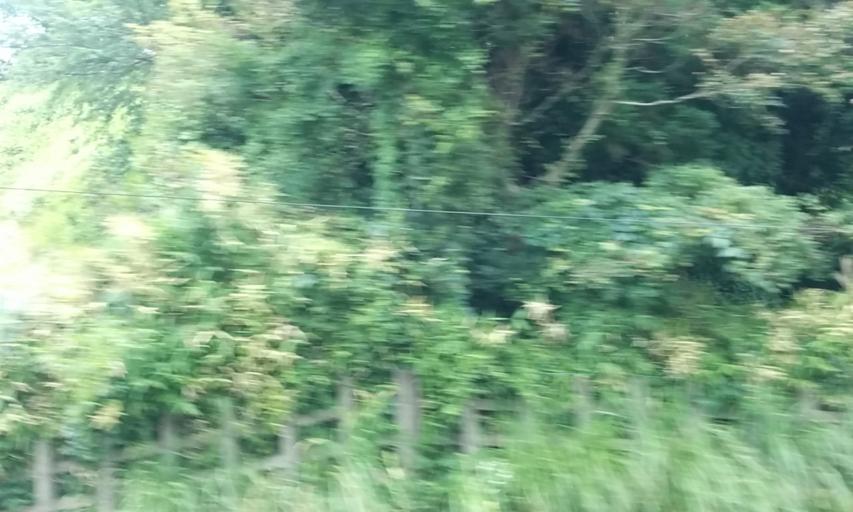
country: JP
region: Chiba
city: Sakura
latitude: 35.7388
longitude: 140.2027
